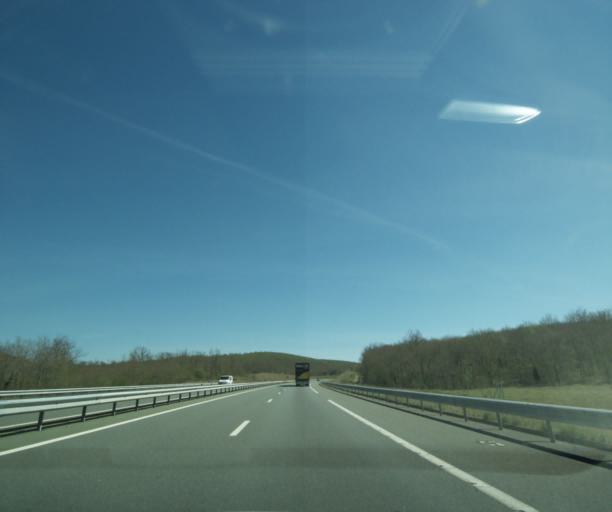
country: FR
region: Midi-Pyrenees
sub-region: Departement du Lot
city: Le Vigan
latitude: 44.7916
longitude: 1.5236
